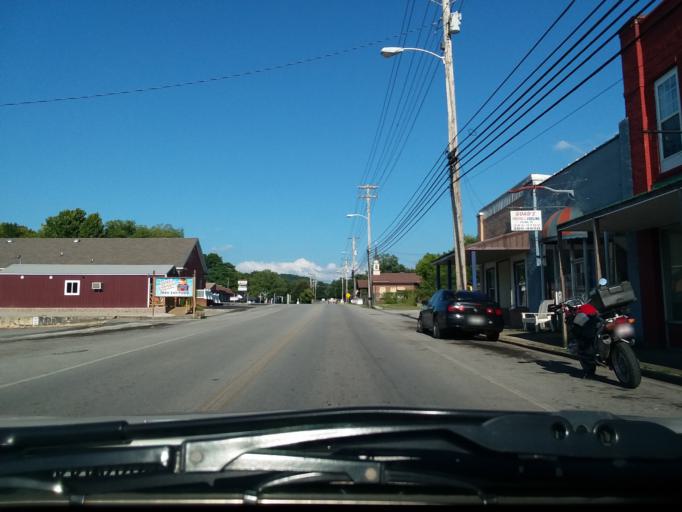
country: US
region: Tennessee
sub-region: Clay County
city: Celina
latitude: 36.5501
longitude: -85.5044
